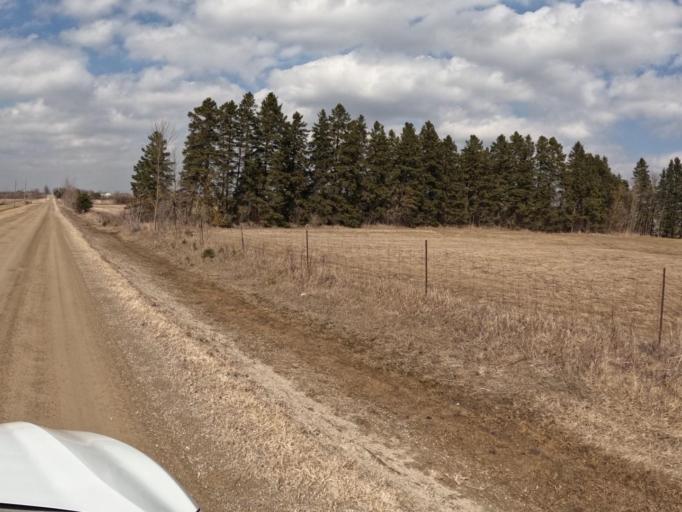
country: CA
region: Ontario
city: Shelburne
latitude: 43.9759
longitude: -80.2683
